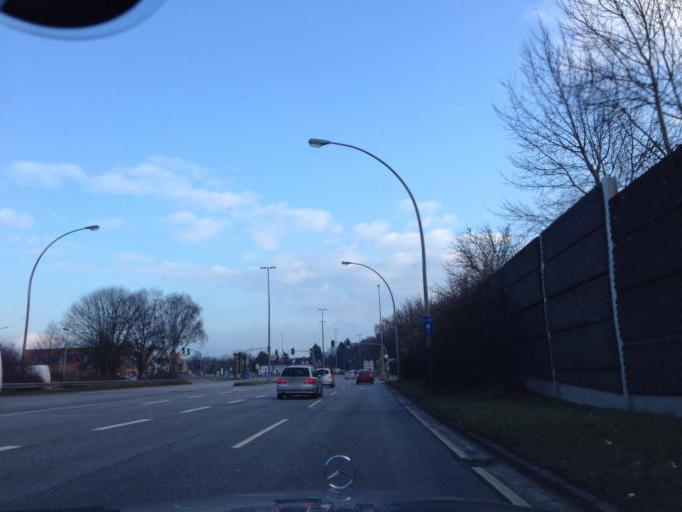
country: DE
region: Schleswig-Holstein
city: Oststeinbek
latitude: 53.5152
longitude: 10.1649
